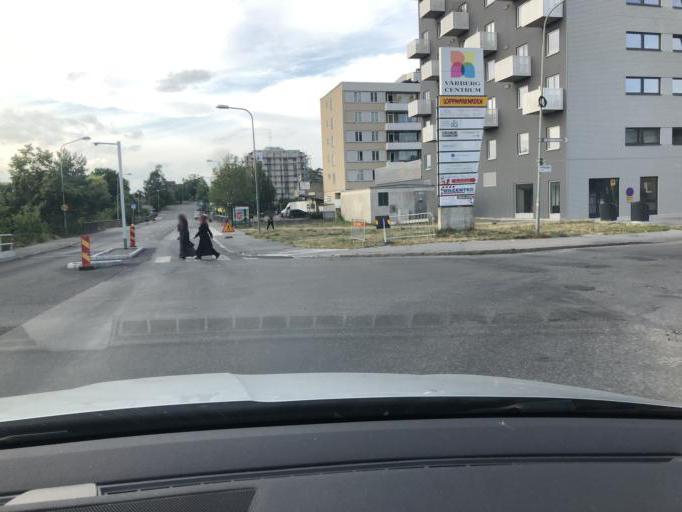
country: SE
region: Stockholm
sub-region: Botkyrka Kommun
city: Fittja
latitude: 59.2752
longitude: 17.8865
